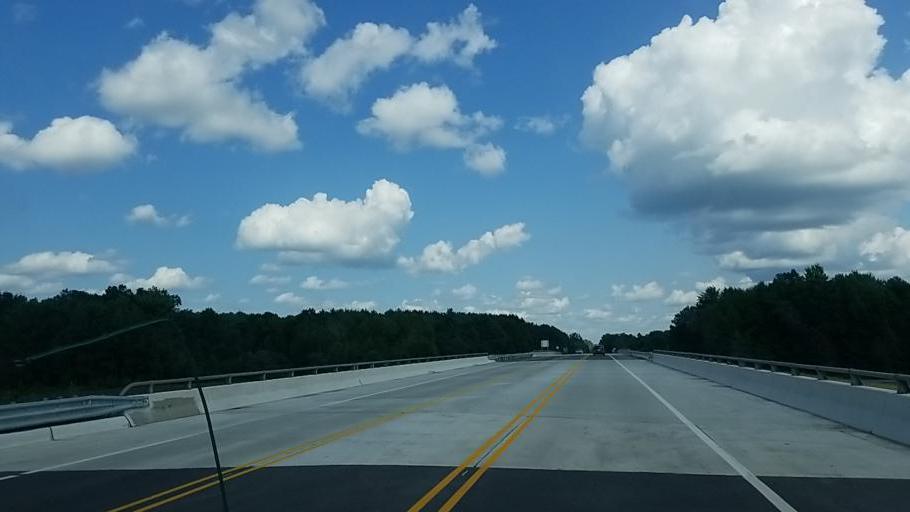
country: US
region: Michigan
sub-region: Montcalm County
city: Howard City
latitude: 43.3957
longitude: -85.5155
